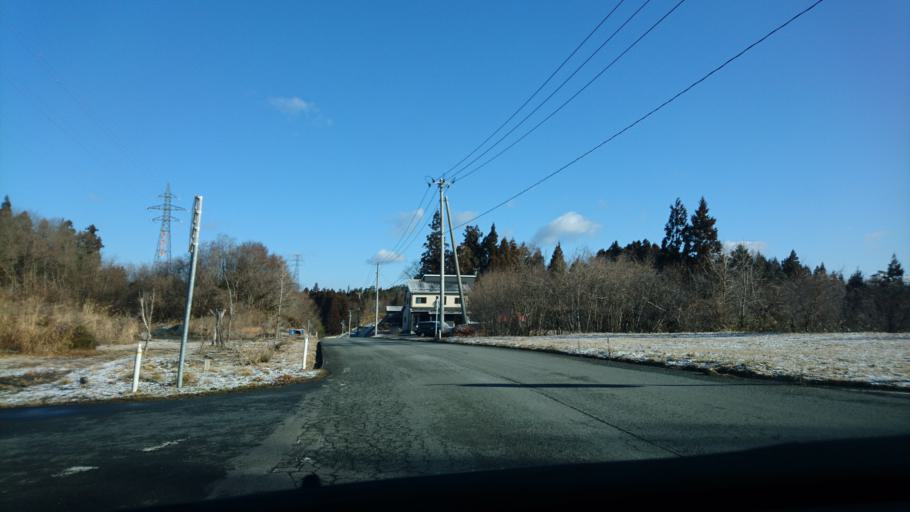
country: JP
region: Iwate
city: Ichinoseki
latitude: 38.8830
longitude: 141.3364
